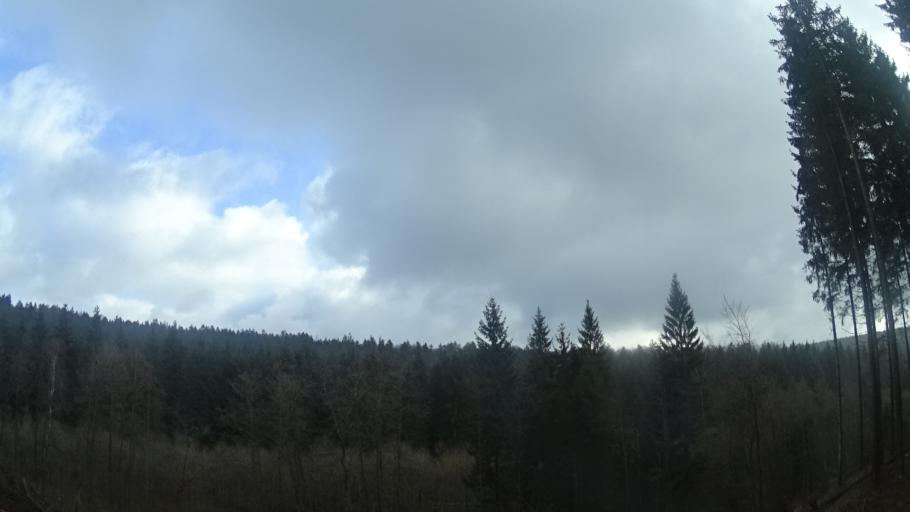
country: DE
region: Rheinland-Pfalz
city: Borfink
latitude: 49.6928
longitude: 7.0807
